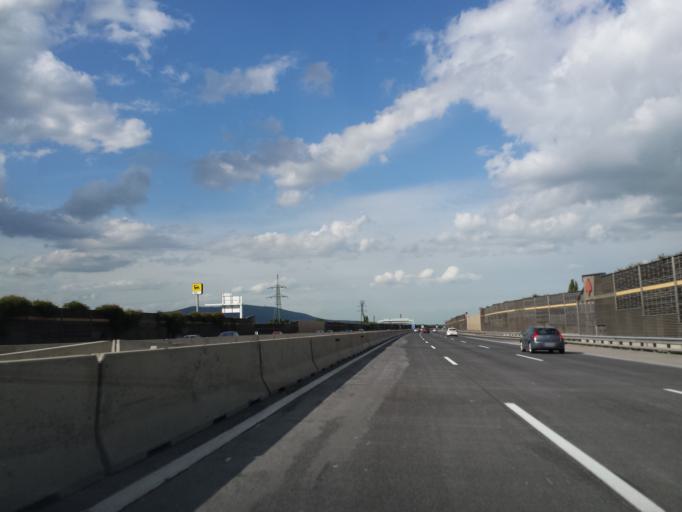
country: AT
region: Lower Austria
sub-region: Politischer Bezirk Baden
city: Kottingbrunn
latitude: 47.9527
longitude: 16.2194
